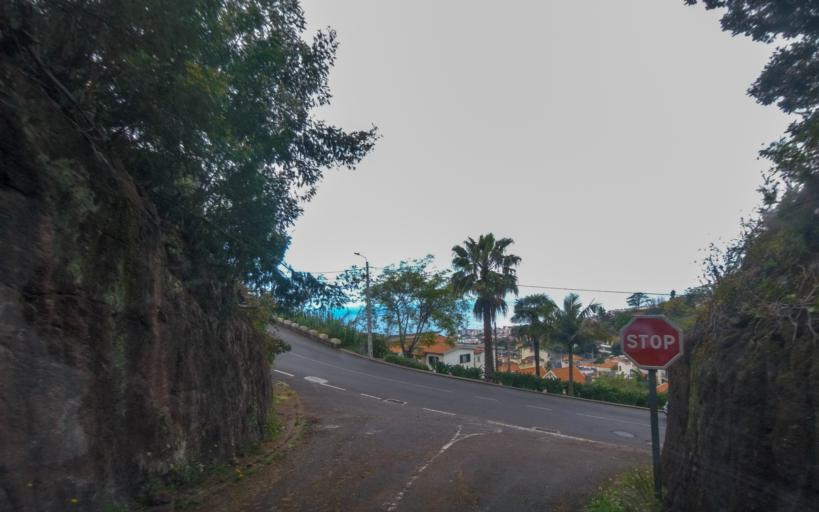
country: PT
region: Madeira
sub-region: Funchal
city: Nossa Senhora do Monte
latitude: 32.6682
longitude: -16.9153
